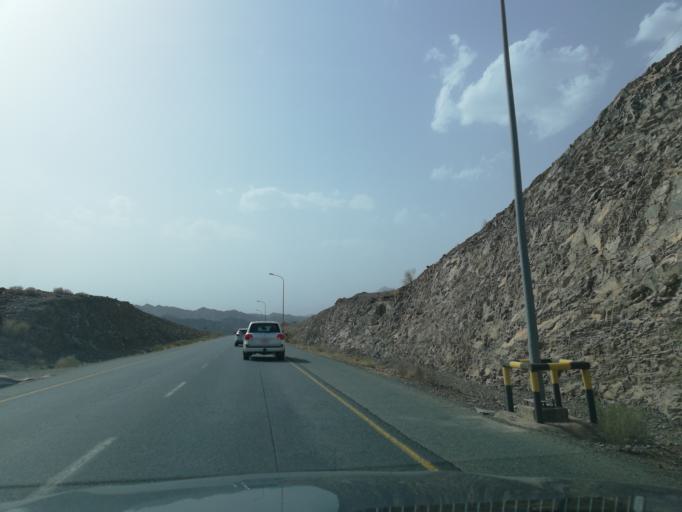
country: OM
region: Muhafazat ad Dakhiliyah
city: Sufalat Sama'il
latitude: 23.1912
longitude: 58.0884
